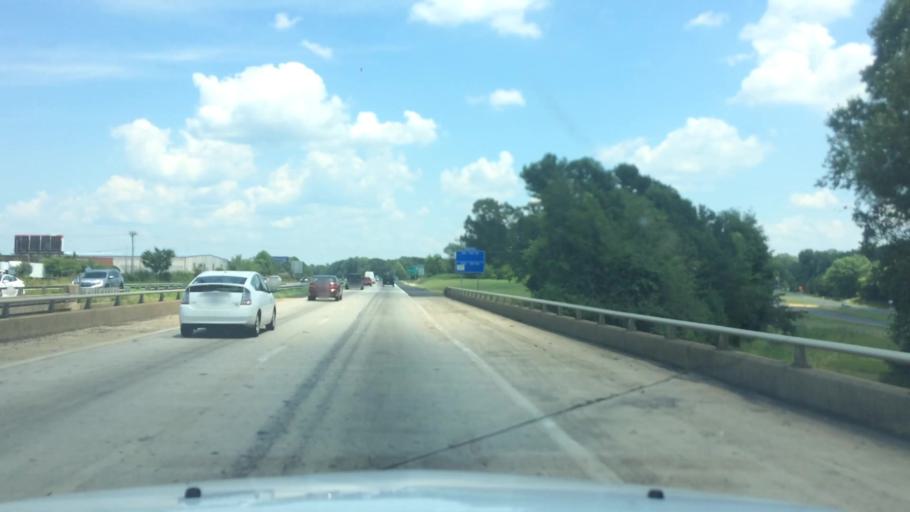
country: US
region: North Carolina
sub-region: Iredell County
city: Statesville
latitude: 35.8126
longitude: -80.8407
